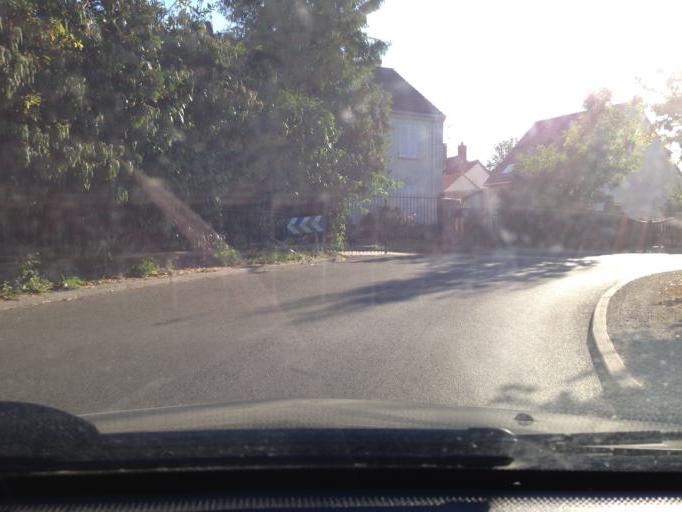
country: FR
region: Ile-de-France
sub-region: Departement des Yvelines
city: Montigny-le-Bretonneux
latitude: 48.7452
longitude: 2.0298
